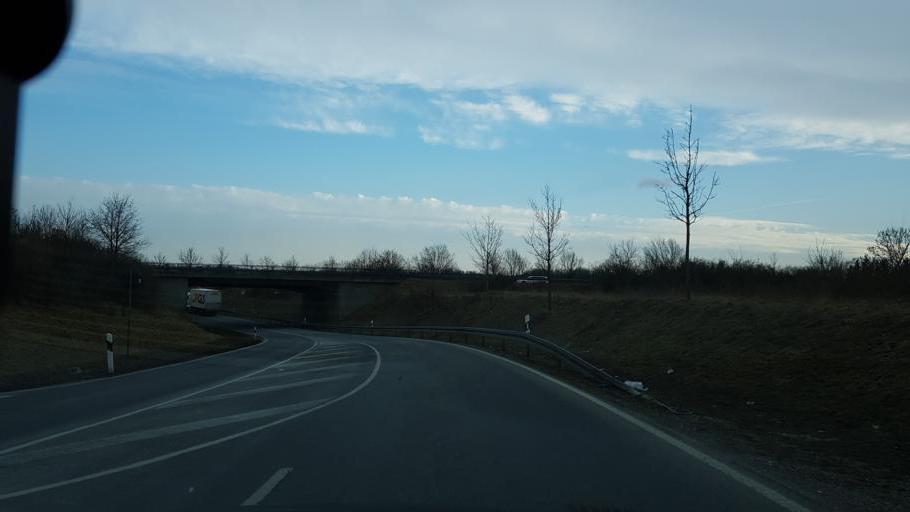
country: DE
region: Bavaria
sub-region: Upper Bavaria
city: Fuerstenfeldbruck
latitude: 48.1856
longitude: 11.2344
